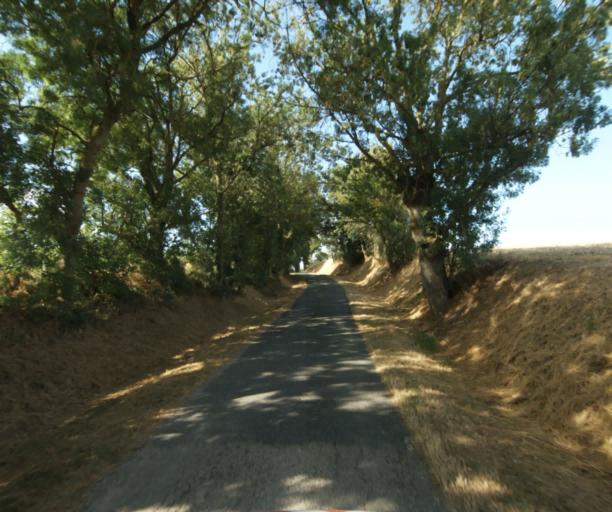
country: FR
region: Midi-Pyrenees
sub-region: Departement du Tarn
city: Puylaurens
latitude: 43.5248
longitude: 1.9893
